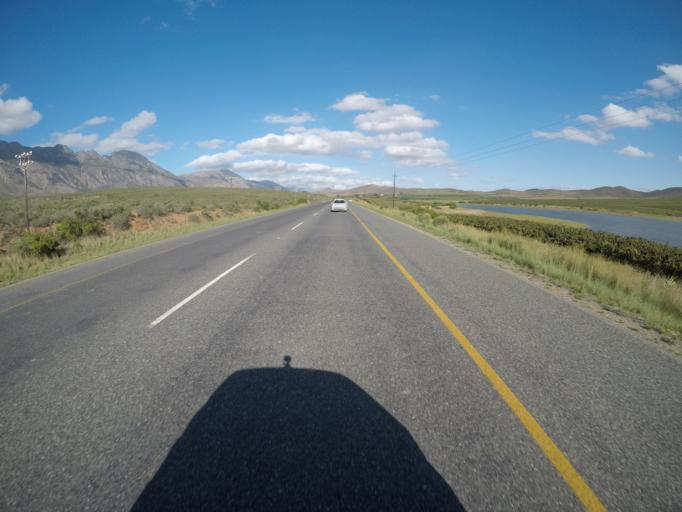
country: ZA
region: Western Cape
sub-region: Cape Winelands District Municipality
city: Ashton
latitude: -33.8516
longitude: 20.1005
